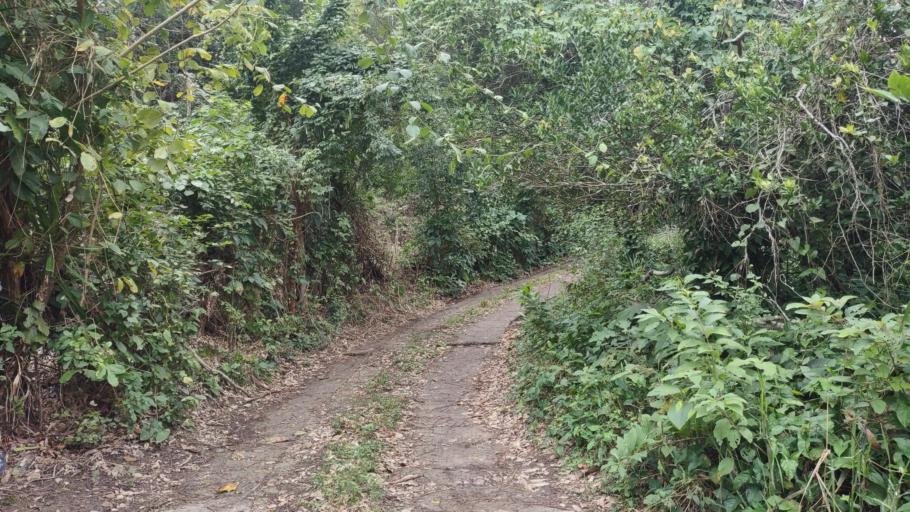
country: MX
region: Veracruz
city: Papantla de Olarte
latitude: 20.4289
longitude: -97.3144
